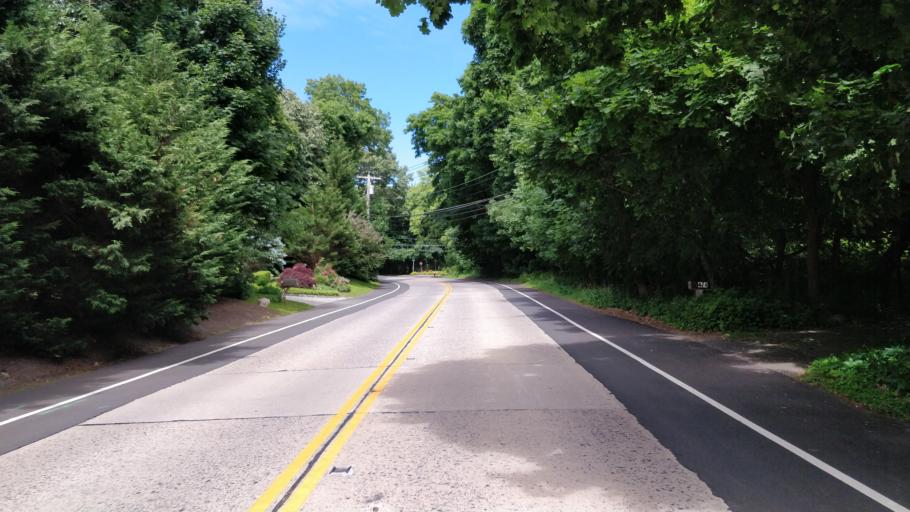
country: US
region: New York
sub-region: Nassau County
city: Laurel Hollow
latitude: 40.8444
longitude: -73.4766
